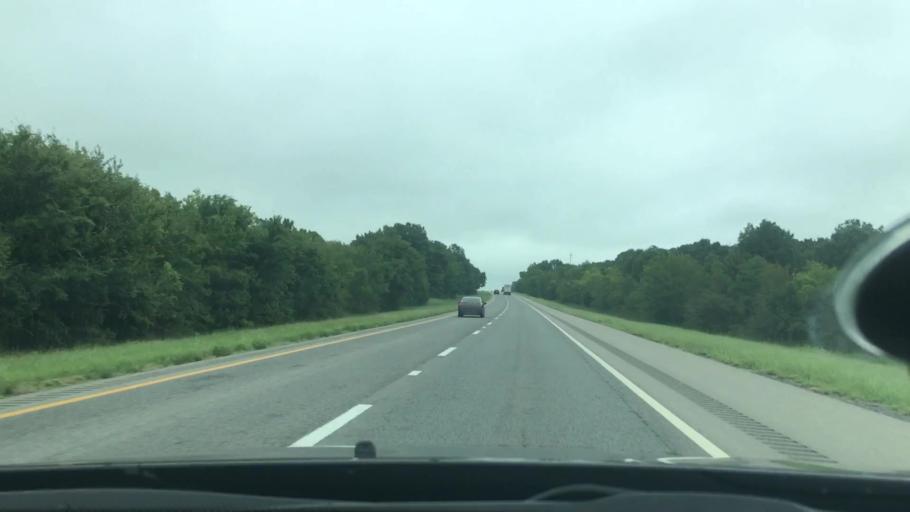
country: US
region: Oklahoma
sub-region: Muskogee County
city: Warner
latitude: 35.4562
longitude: -95.3941
